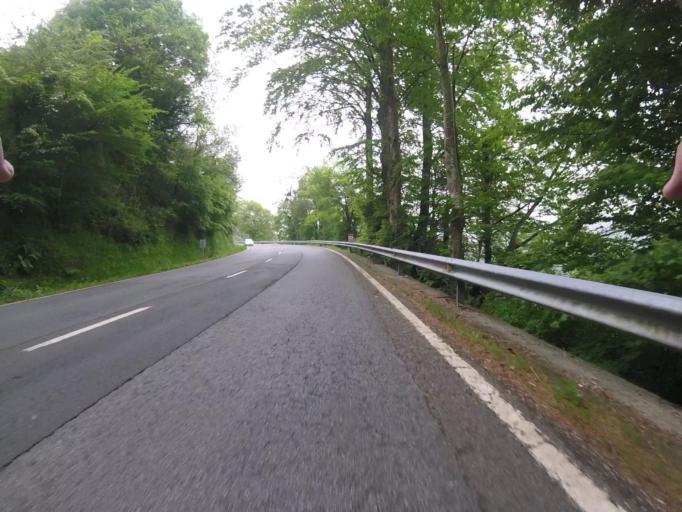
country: ES
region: Navarre
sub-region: Provincia de Navarra
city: Zugarramurdi
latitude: 43.2515
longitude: -1.4834
